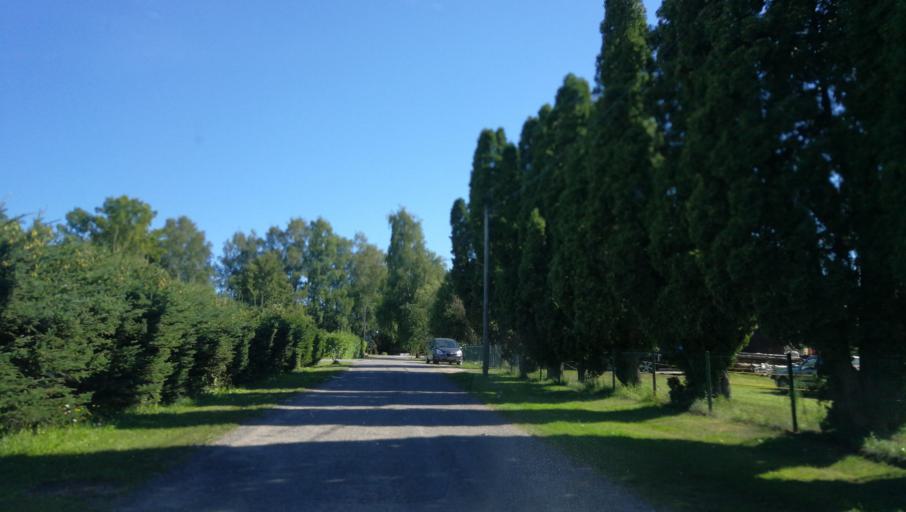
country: LV
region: Cesu Rajons
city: Cesis
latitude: 57.3027
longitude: 25.2495
